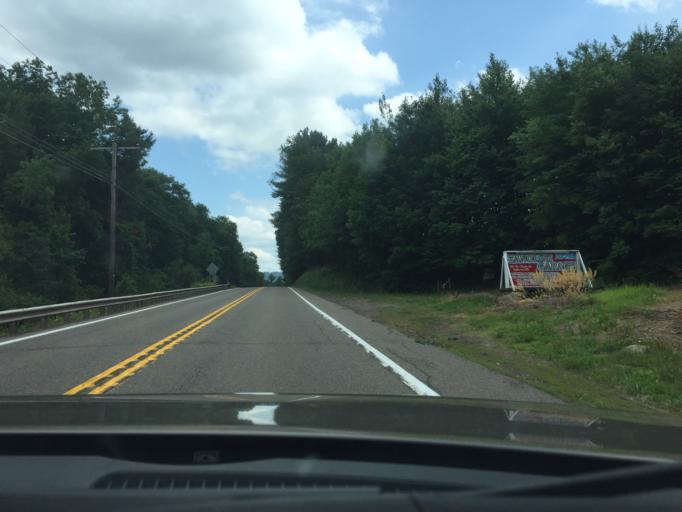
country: US
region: Pennsylvania
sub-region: Luzerne County
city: Conyngham
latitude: 41.0131
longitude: -76.0783
